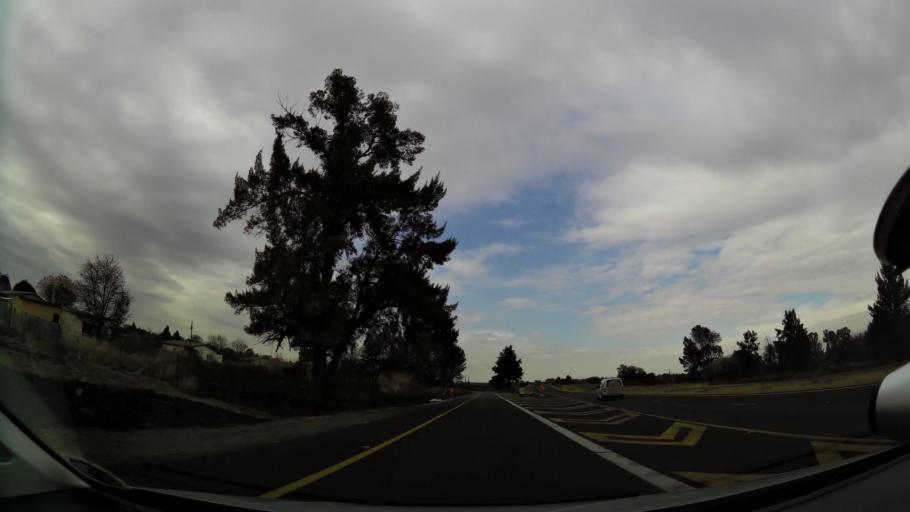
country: ZA
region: Orange Free State
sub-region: Fezile Dabi District Municipality
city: Kroonstad
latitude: -27.6542
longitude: 27.2491
